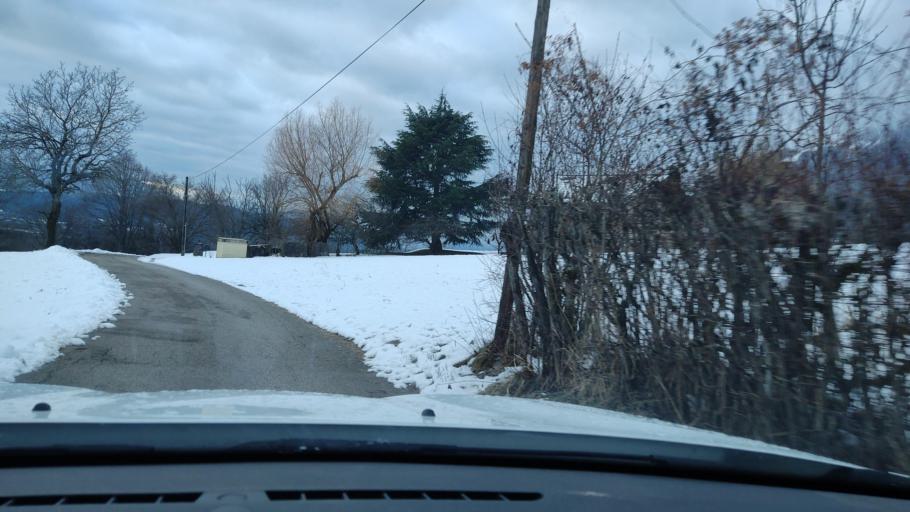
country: FR
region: Rhone-Alpes
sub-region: Departement de la Savoie
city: Coise-Saint-Jean-Pied-Gauthier
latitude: 45.5775
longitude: 6.1474
